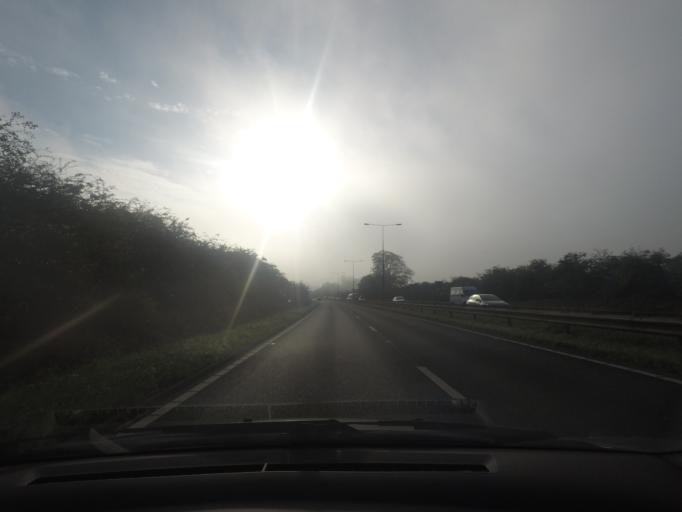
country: GB
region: England
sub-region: East Riding of Yorkshire
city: Welton
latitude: 53.7364
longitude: -0.5608
